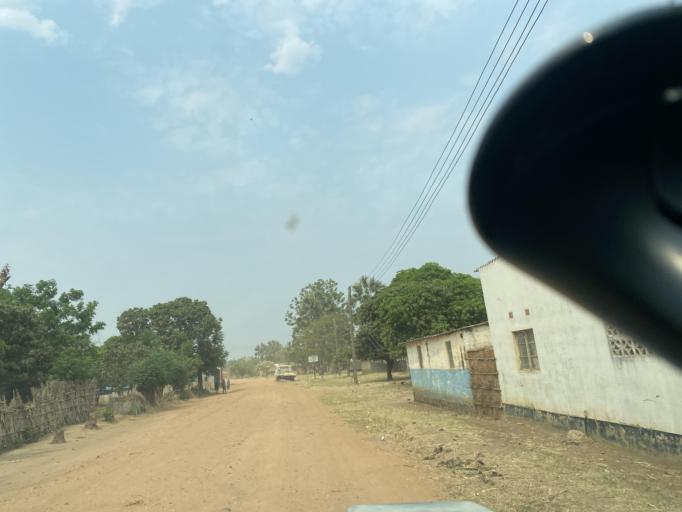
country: ZM
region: Lusaka
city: Kafue
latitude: -15.6646
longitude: 28.0199
